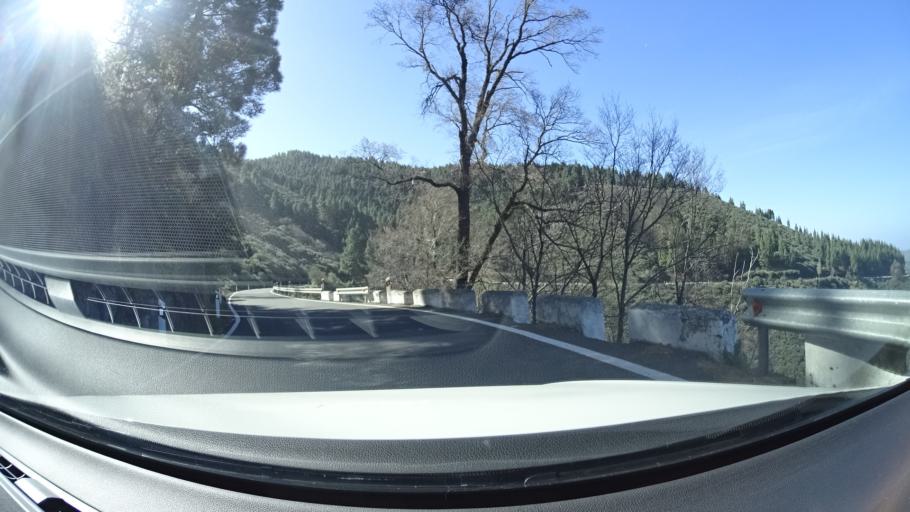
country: ES
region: Canary Islands
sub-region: Provincia de Las Palmas
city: Artenara
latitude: 28.0282
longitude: -15.6181
